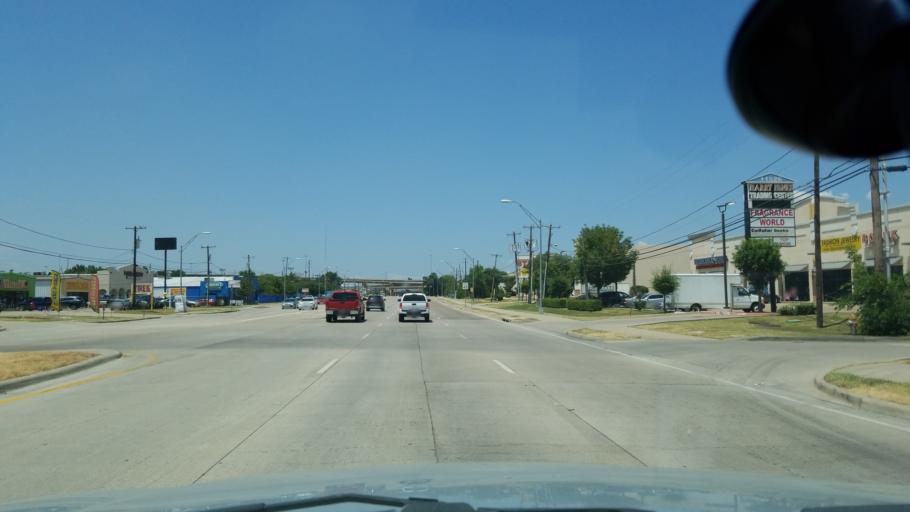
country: US
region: Texas
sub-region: Dallas County
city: Farmers Branch
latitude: 32.8997
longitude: -96.8925
